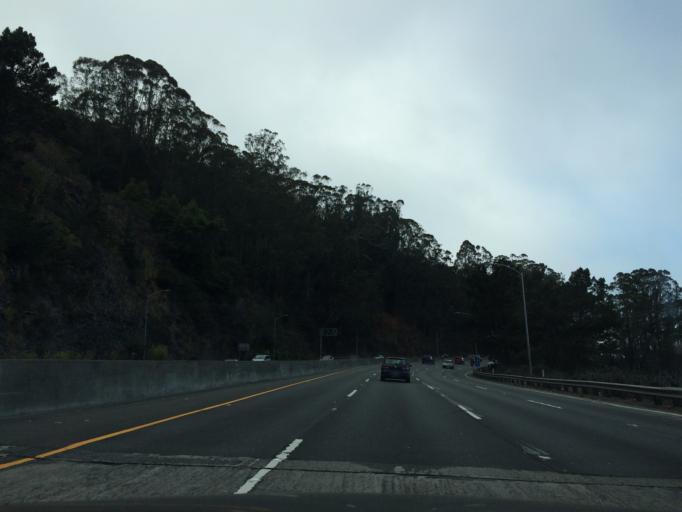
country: US
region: California
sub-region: Marin County
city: Sausalito
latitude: 37.8478
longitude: -122.4879
